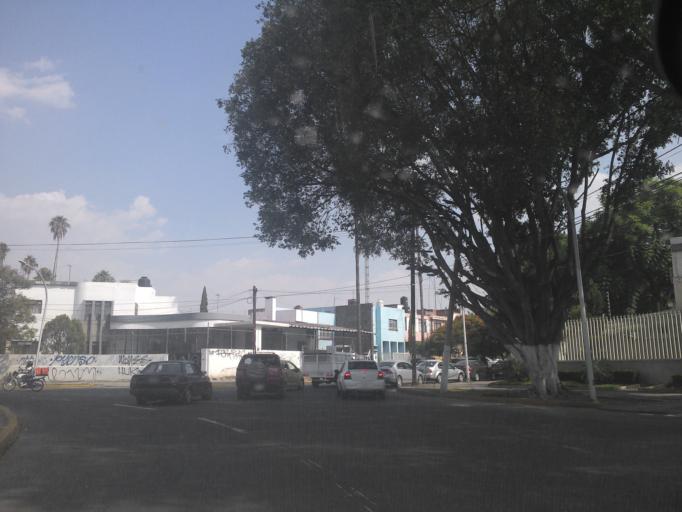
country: MX
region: Jalisco
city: Guadalajara
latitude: 20.6621
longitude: -103.3609
